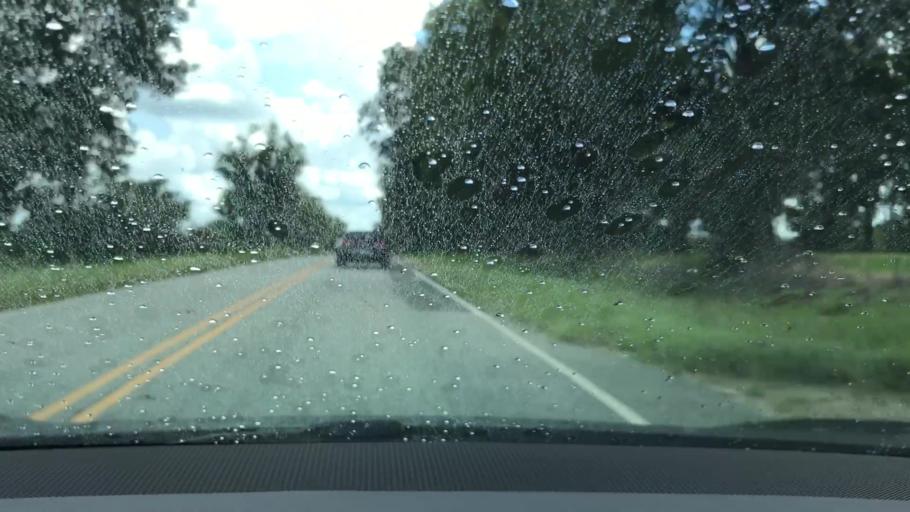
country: US
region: Alabama
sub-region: Montgomery County
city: Pike Road
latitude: 32.2418
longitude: -86.0932
